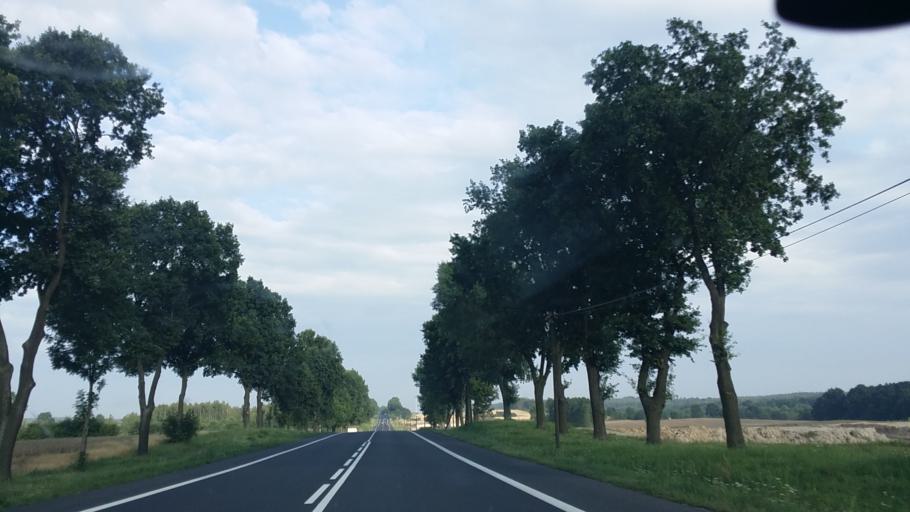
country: PL
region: Lubusz
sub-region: Powiat nowosolski
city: Nowe Miasteczko
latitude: 51.6782
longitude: 15.7774
